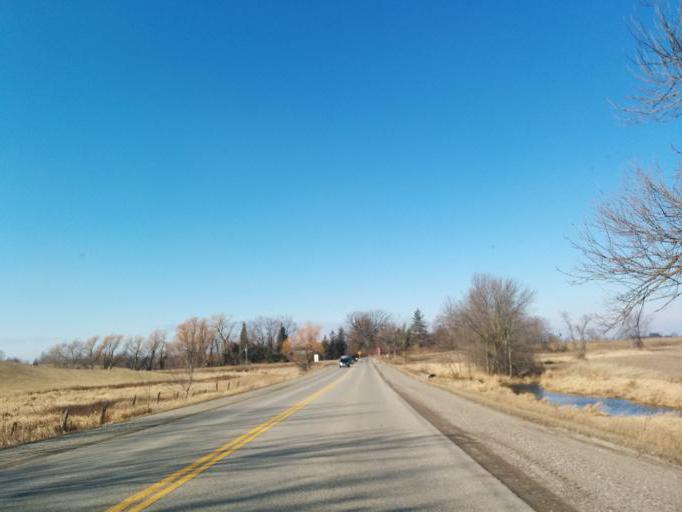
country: CA
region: Ontario
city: Brantford
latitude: 43.0415
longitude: -80.2698
